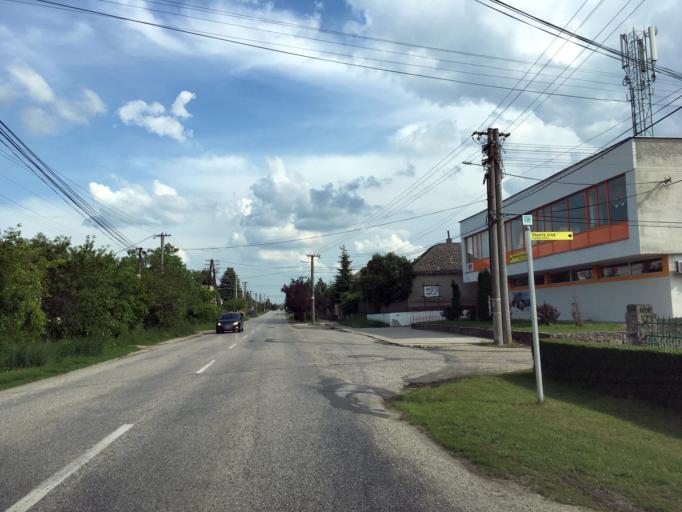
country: SK
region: Nitriansky
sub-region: Okres Komarno
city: Hurbanovo
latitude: 47.8056
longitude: 18.2312
